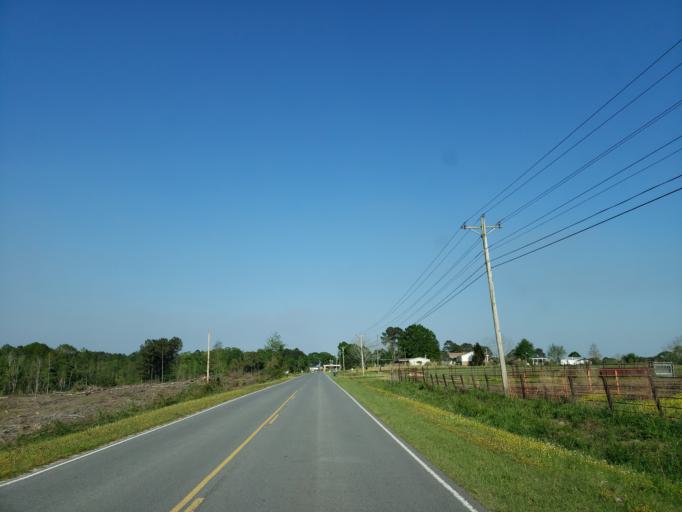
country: US
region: Mississippi
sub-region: Perry County
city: Richton
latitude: 31.4818
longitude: -89.0227
